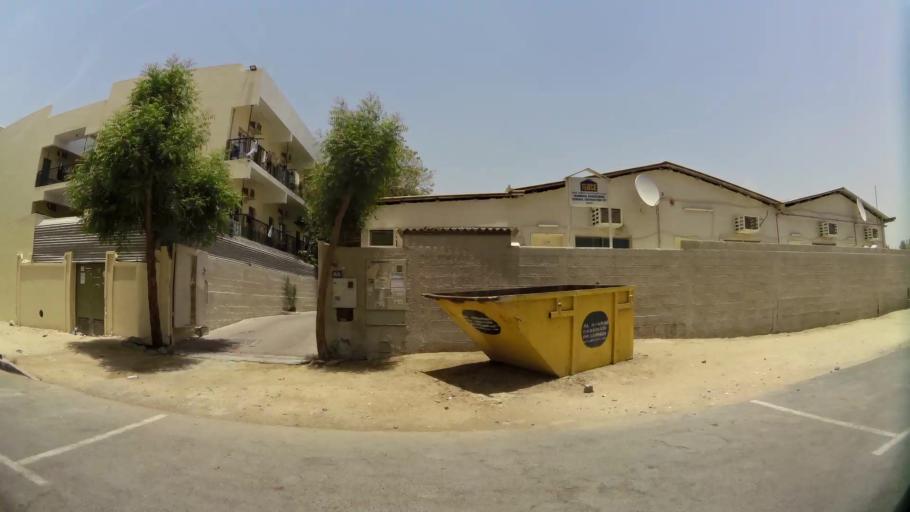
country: AE
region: Ash Shariqah
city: Sharjah
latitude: 25.2683
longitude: 55.4328
